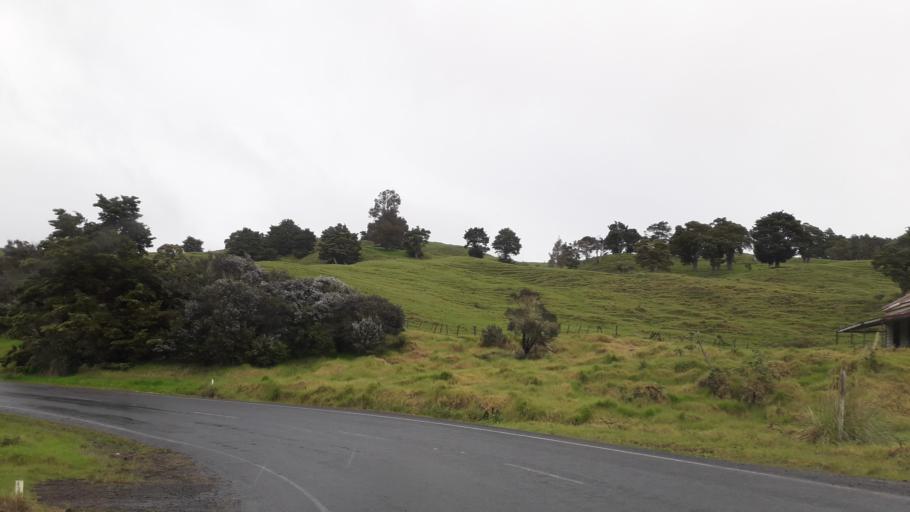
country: NZ
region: Northland
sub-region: Far North District
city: Kaitaia
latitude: -35.3603
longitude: 173.4942
